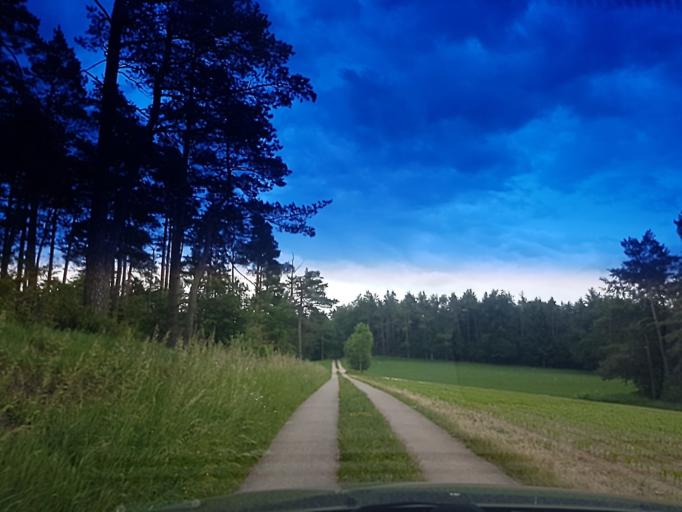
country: DE
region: Bavaria
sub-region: Upper Franconia
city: Wattendorf
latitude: 50.0088
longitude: 11.1240
